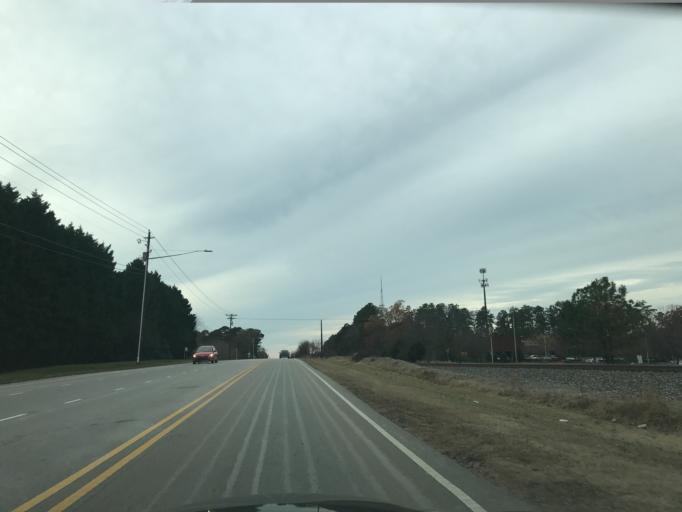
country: US
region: North Carolina
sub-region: Wake County
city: Cary
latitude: 35.7900
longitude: -78.7505
